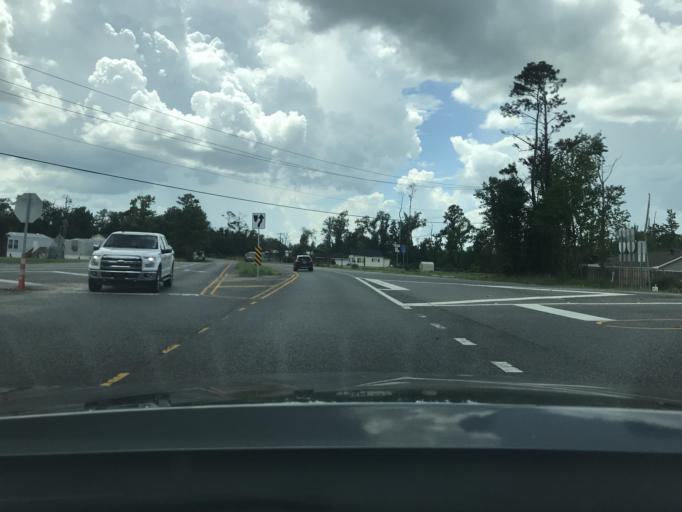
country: US
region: Louisiana
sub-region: Calcasieu Parish
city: Moss Bluff
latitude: 30.3007
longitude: -93.2444
